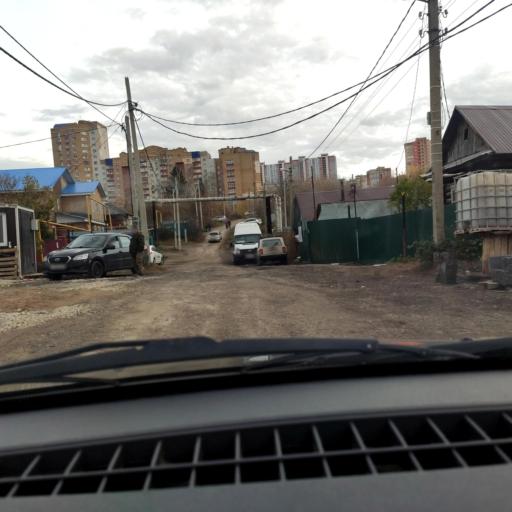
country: RU
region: Bashkortostan
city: Ufa
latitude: 54.7263
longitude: 56.0098
